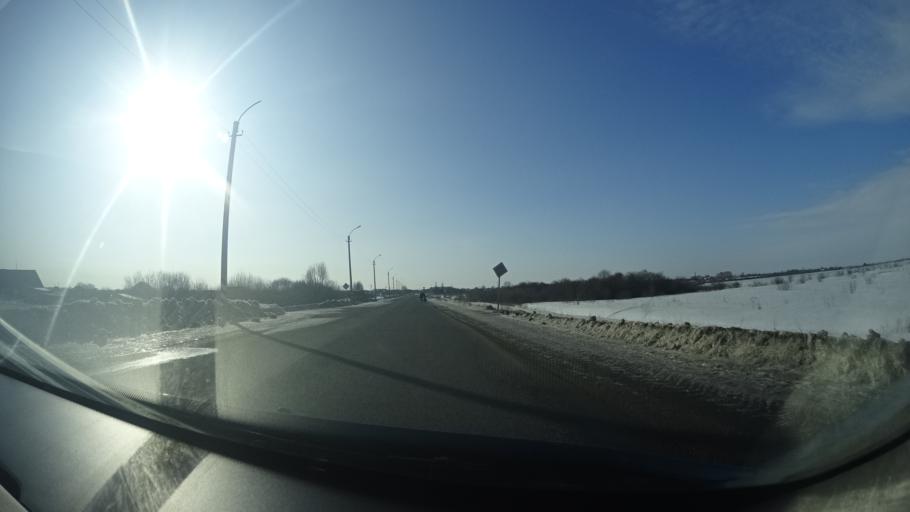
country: RU
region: Perm
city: Kuyeda
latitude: 56.4527
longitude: 55.6010
